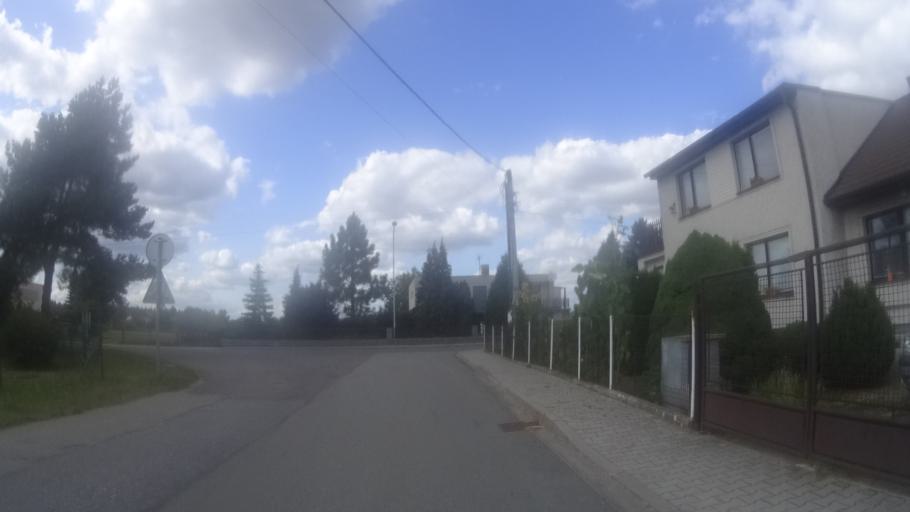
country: CZ
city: Borohradek
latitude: 50.0761
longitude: 16.1322
